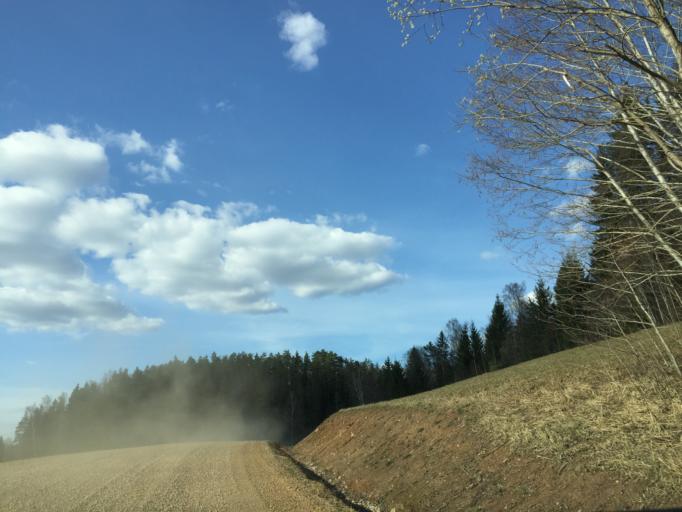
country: EE
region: Tartu
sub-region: Elva linn
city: Elva
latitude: 58.0994
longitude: 26.5075
